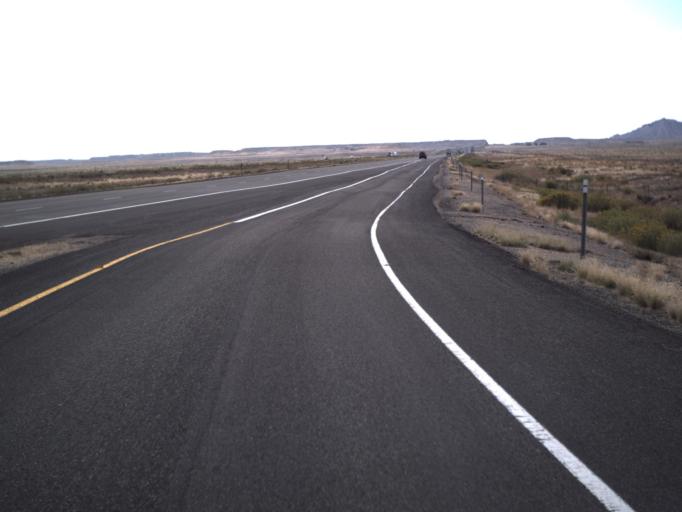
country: US
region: Utah
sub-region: Grand County
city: Moab
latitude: 38.9547
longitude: -109.7577
